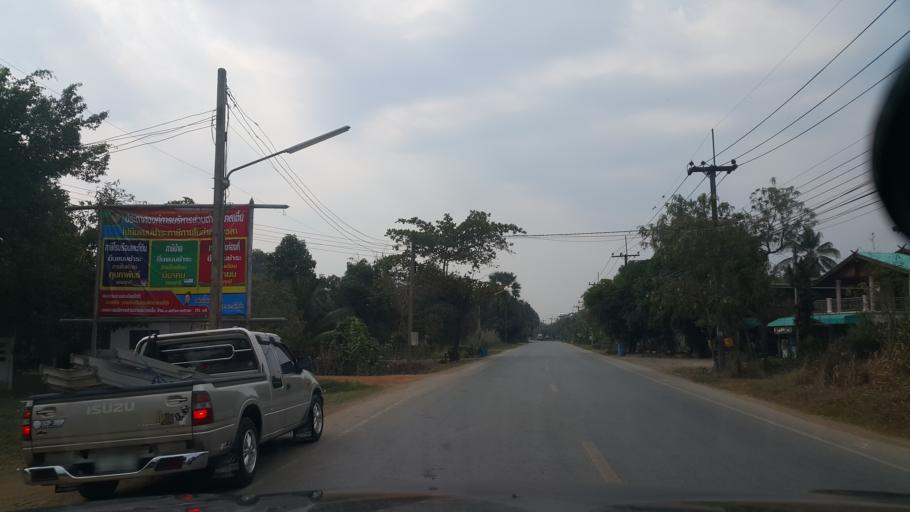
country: TH
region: Sukhothai
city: Si Samrong
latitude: 17.0870
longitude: 99.8832
